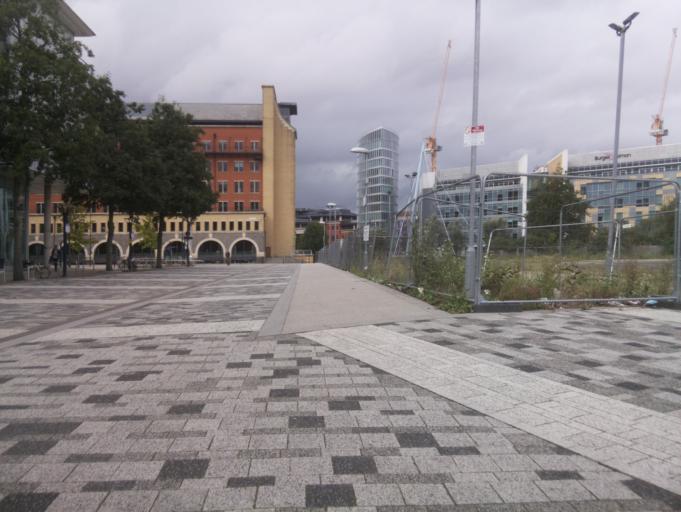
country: GB
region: England
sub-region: Bristol
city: Bristol
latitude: 51.4505
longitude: -2.5815
